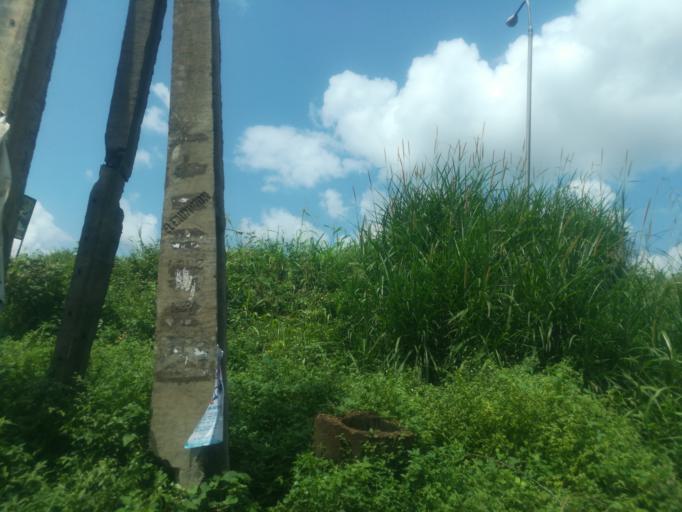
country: NG
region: Oyo
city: Lalupon
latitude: 7.4326
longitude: 4.0032
